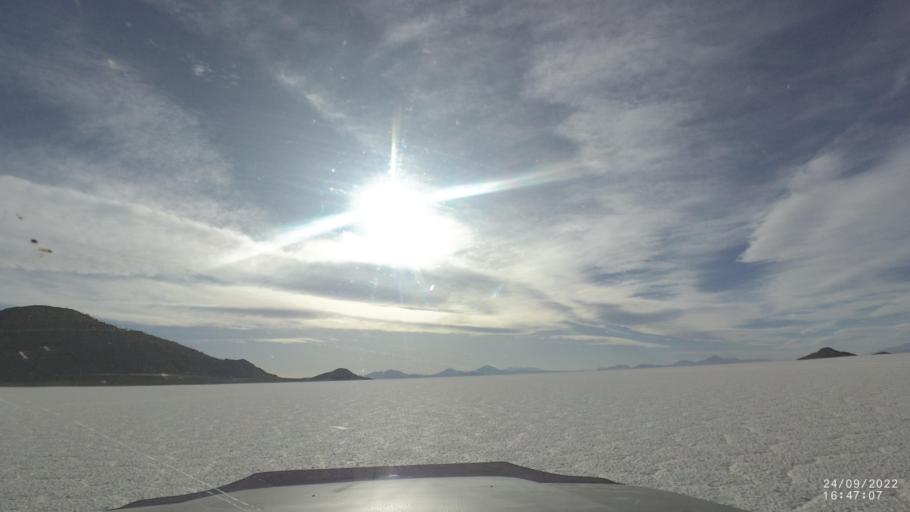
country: BO
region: Potosi
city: Colchani
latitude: -20.1330
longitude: -67.7991
